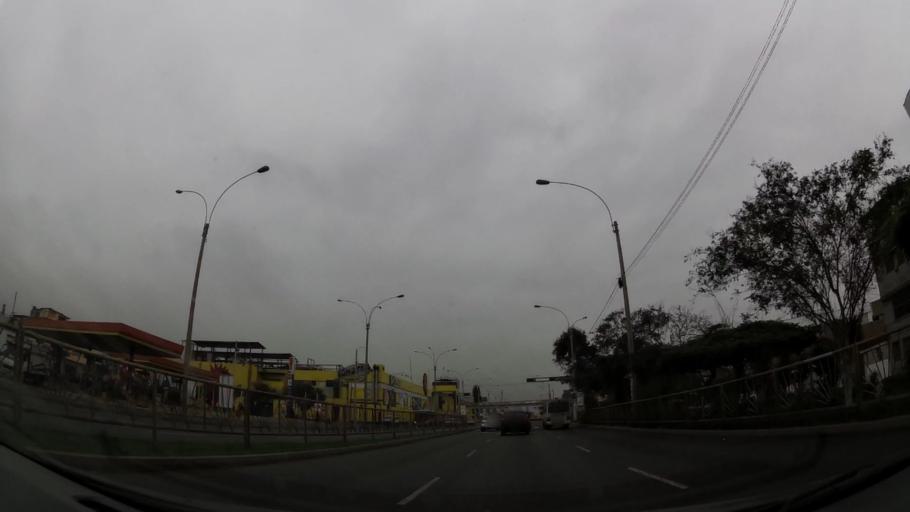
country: PE
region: Lima
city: Lima
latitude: -12.0580
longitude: -77.0690
